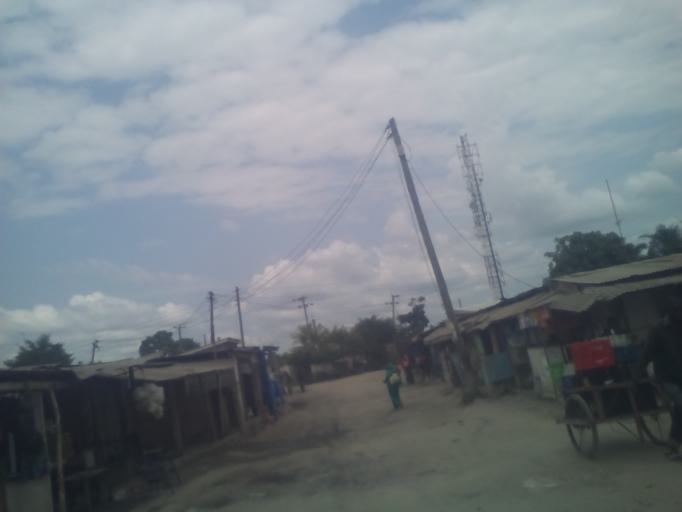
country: TZ
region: Dar es Salaam
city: Dar es Salaam
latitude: -6.8689
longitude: 39.2306
